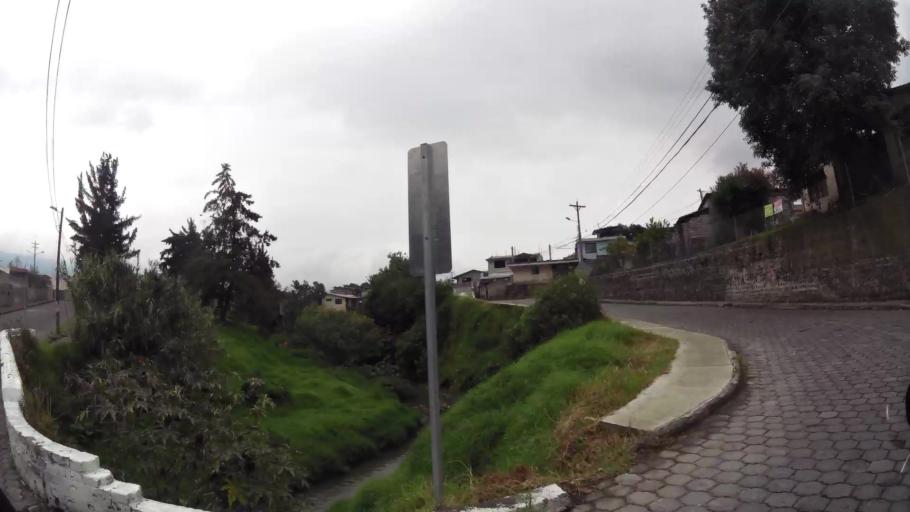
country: EC
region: Pichincha
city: Sangolqui
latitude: -0.3134
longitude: -78.4597
